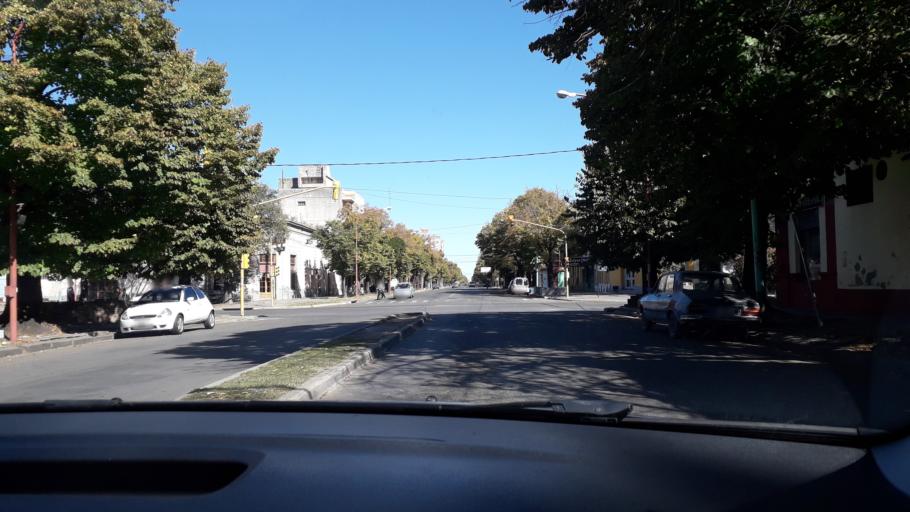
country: AR
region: Buenos Aires
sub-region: Partido de Azul
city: Azul
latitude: -36.7777
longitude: -59.8581
